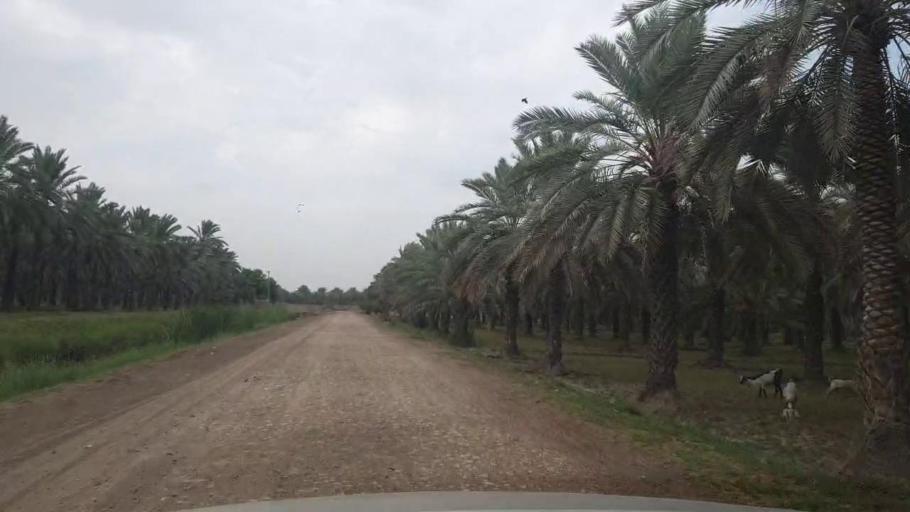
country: PK
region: Sindh
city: Sukkur
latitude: 27.6092
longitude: 68.8354
